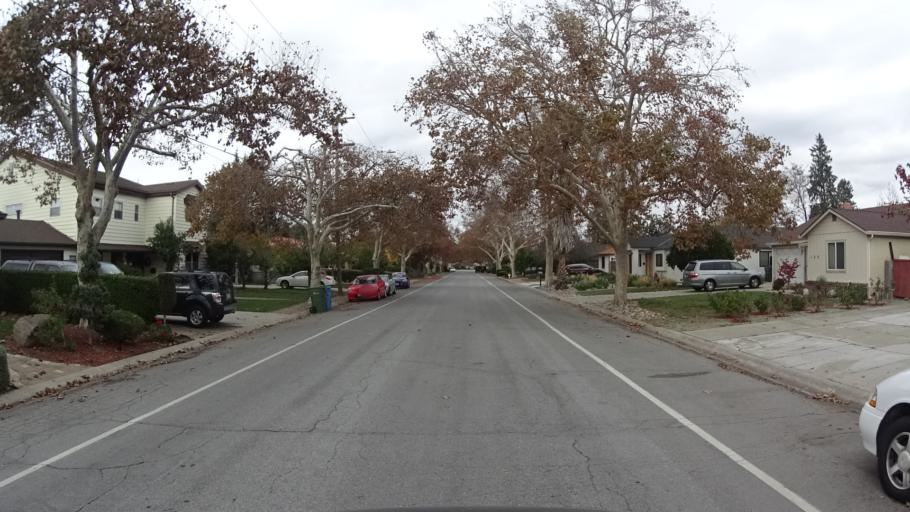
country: US
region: California
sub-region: Santa Clara County
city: Cupertino
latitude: 37.3251
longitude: -121.9906
